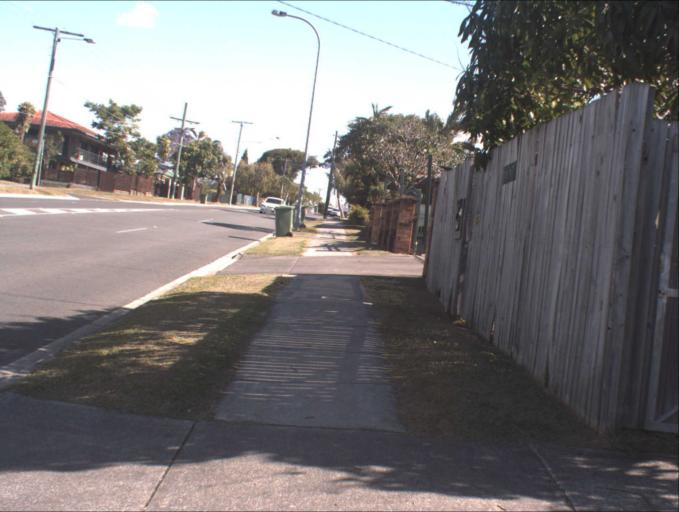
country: AU
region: Queensland
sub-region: Logan
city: Rochedale South
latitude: -27.5961
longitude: 153.1218
